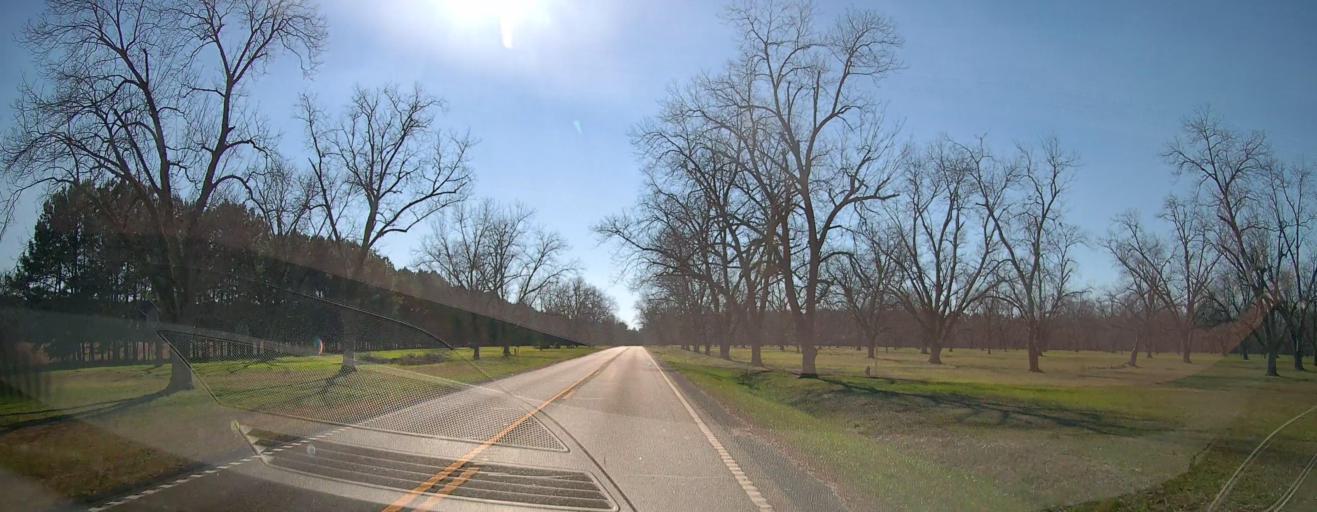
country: US
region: Georgia
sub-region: Schley County
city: Ellaville
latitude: 32.1862
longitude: -84.2421
